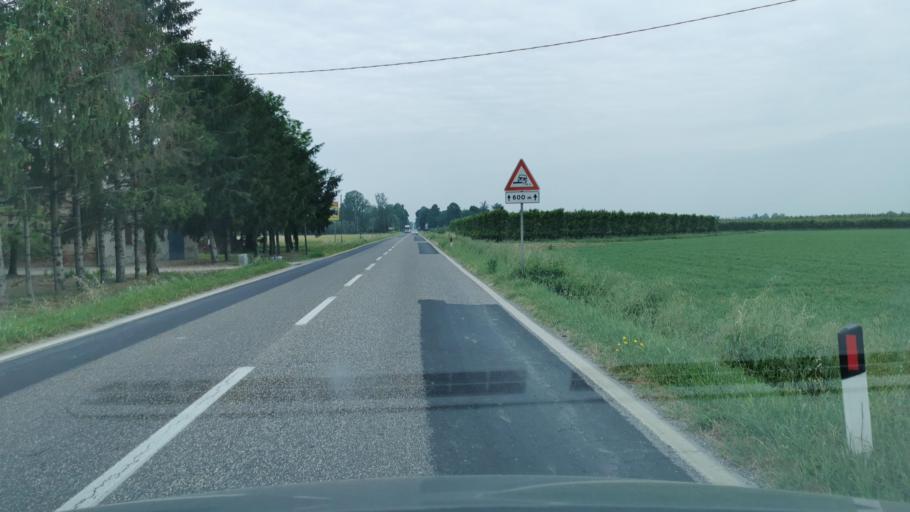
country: IT
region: Emilia-Romagna
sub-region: Provincia di Ravenna
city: Russi
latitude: 44.3919
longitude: 12.0469
